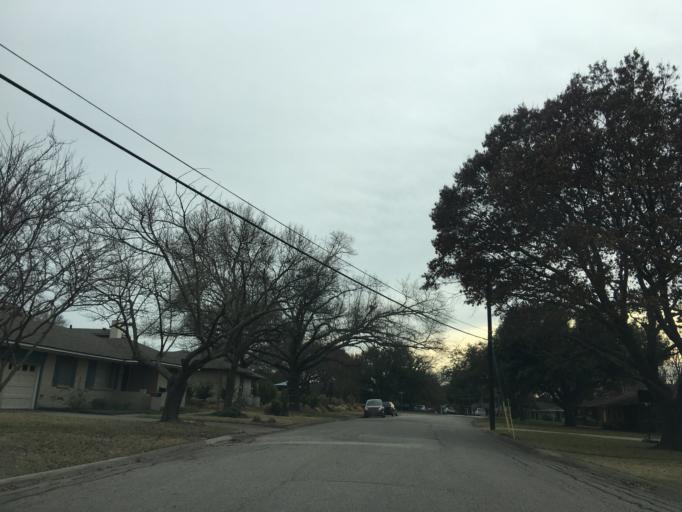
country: US
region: Texas
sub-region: Collin County
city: McKinney
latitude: 33.2036
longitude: -96.6314
